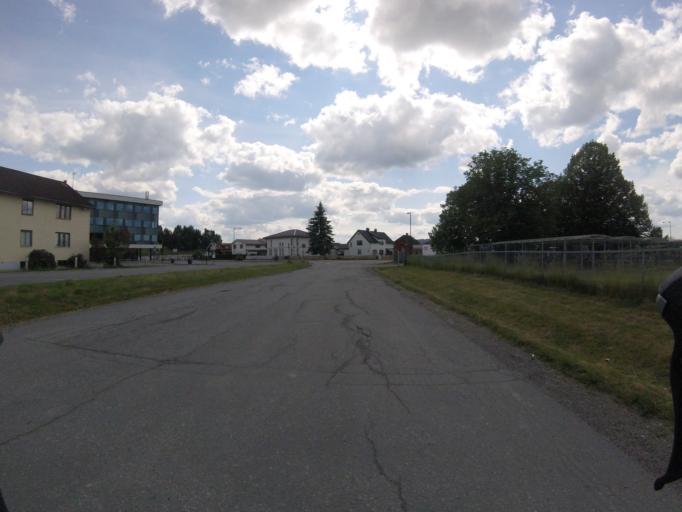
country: NO
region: Akershus
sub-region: Skedsmo
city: Lillestrom
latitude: 59.9744
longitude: 11.0463
